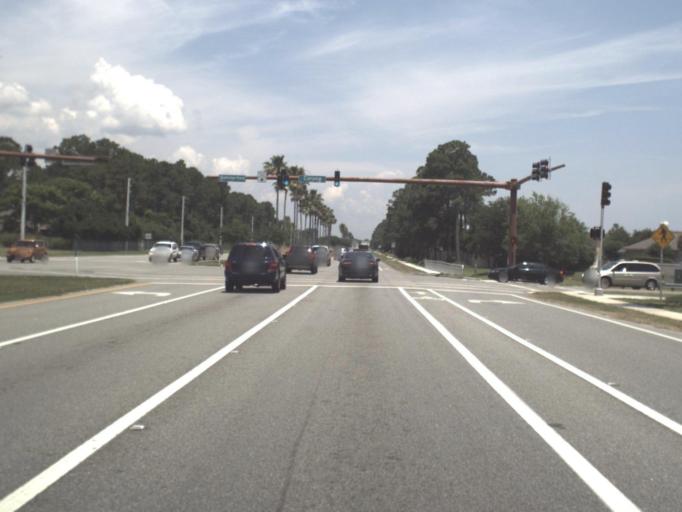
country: US
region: Florida
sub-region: Saint Johns County
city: Ponte Vedra Beach
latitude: 30.2162
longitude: -81.3812
